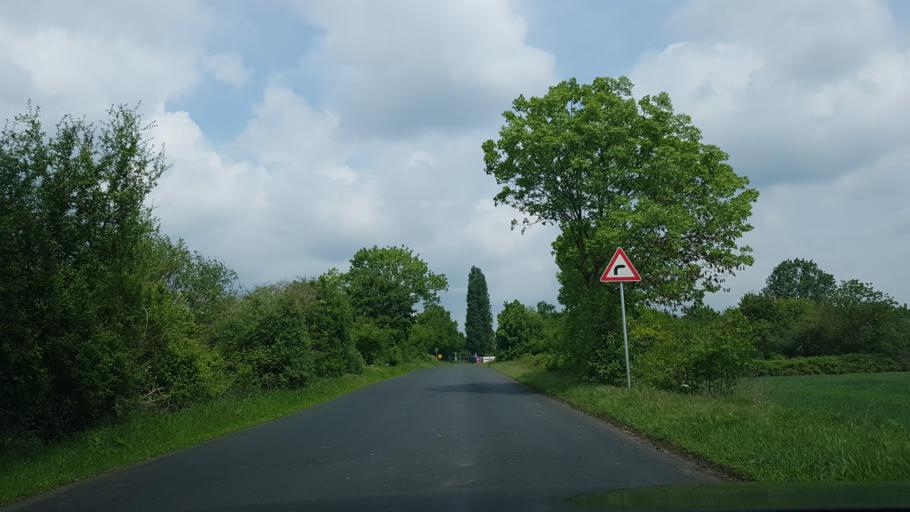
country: DE
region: North Rhine-Westphalia
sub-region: Regierungsbezirk Dusseldorf
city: Moers
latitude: 51.4234
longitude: 6.6659
